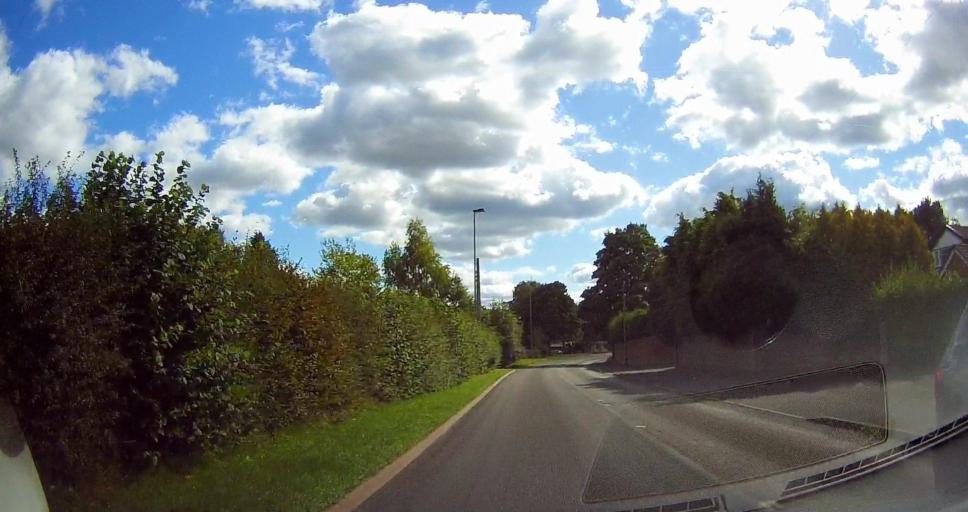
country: GB
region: England
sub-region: Cheshire East
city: Chorlton
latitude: 52.9669
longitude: -2.3951
